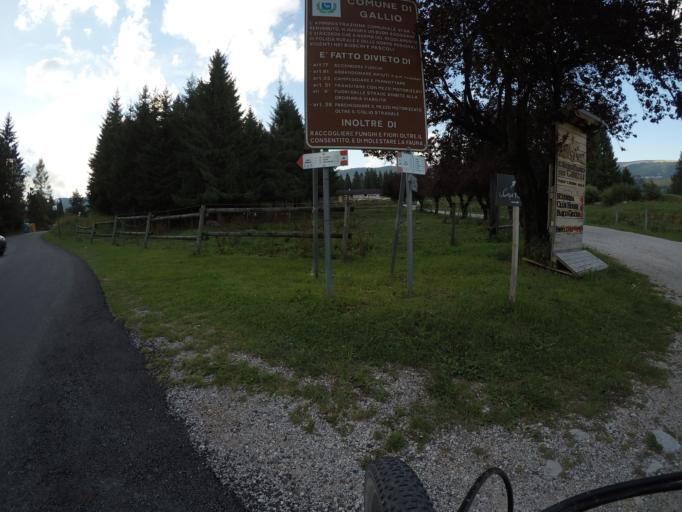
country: IT
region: Veneto
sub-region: Provincia di Vicenza
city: Gallio
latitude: 45.8914
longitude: 11.5385
